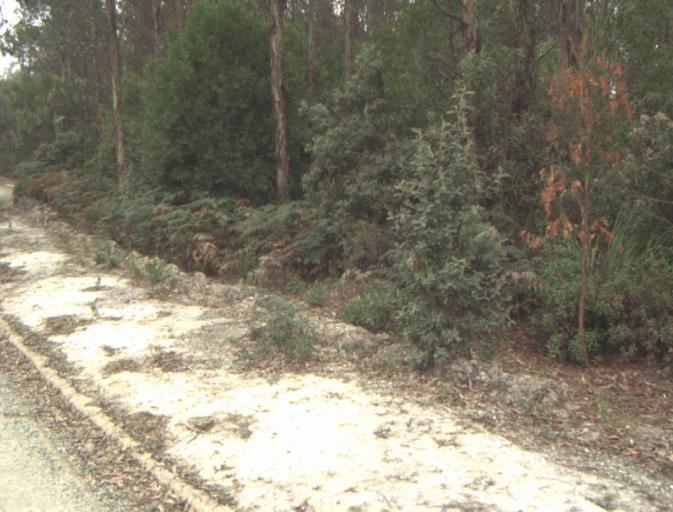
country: AU
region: Tasmania
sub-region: Launceston
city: Mayfield
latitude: -41.1662
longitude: 147.1810
